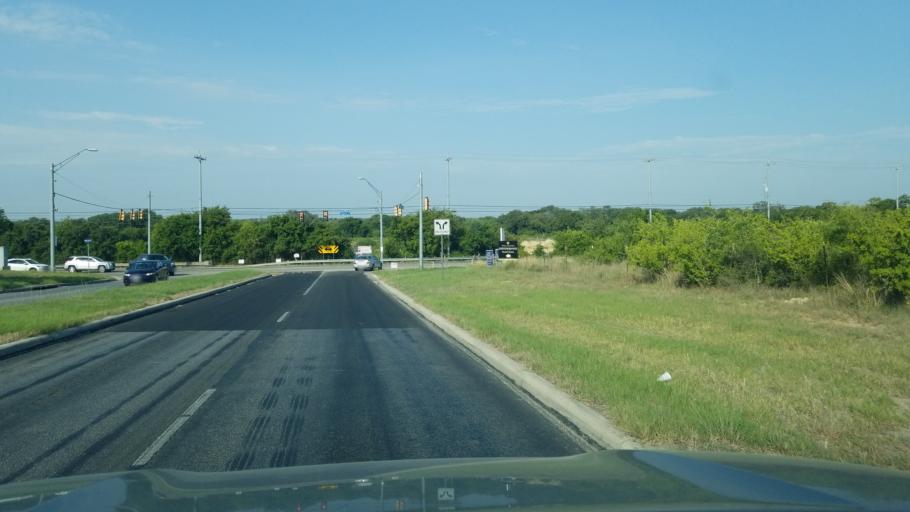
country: US
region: Texas
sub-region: Bexar County
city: Helotes
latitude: 29.4617
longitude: -98.7577
